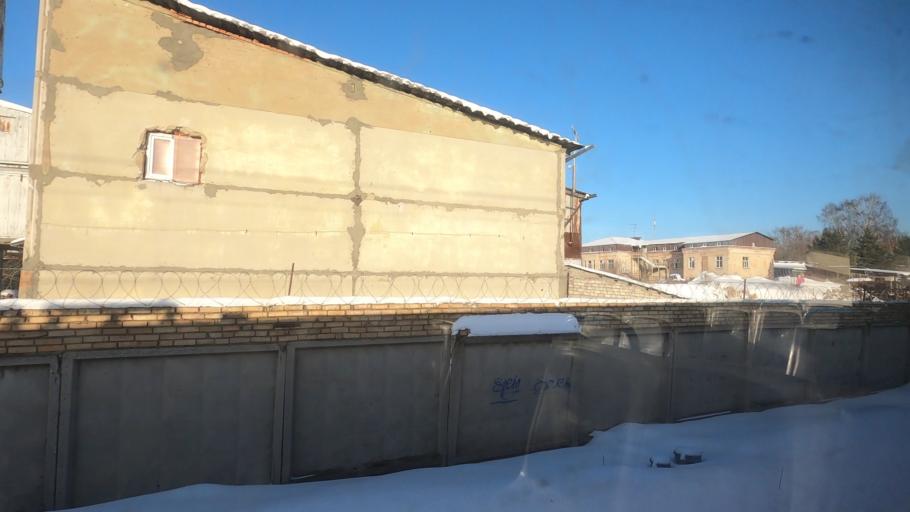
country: RU
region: Moskovskaya
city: Pavlovskiy Posad
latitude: 55.7743
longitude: 38.6952
